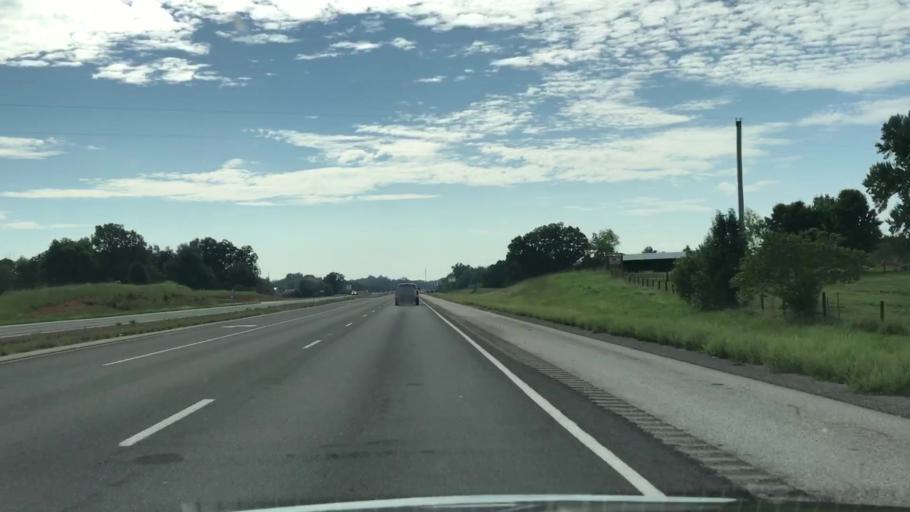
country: US
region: Kentucky
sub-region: Warren County
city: Plano
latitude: 36.8407
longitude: -86.3240
